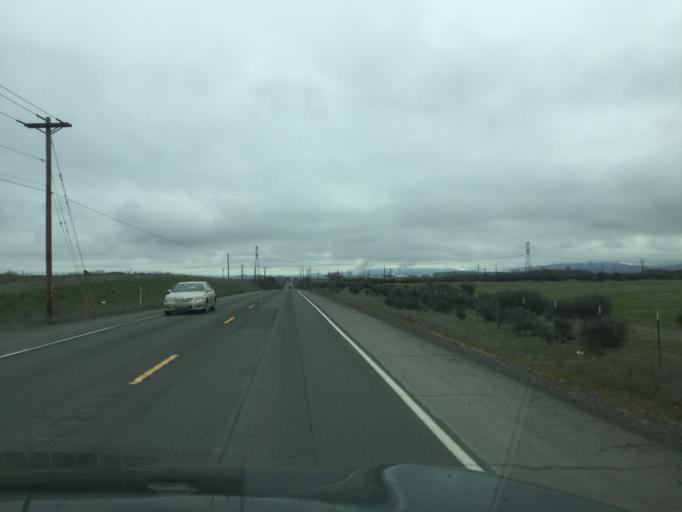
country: US
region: Oregon
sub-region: Jackson County
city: Central Point
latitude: 42.4299
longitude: -122.9248
